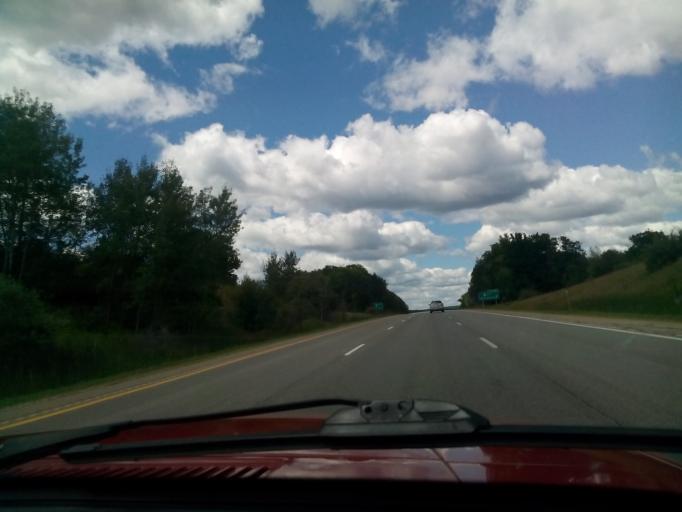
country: US
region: Michigan
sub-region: Ogemaw County
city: West Branch
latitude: 44.2679
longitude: -84.2717
